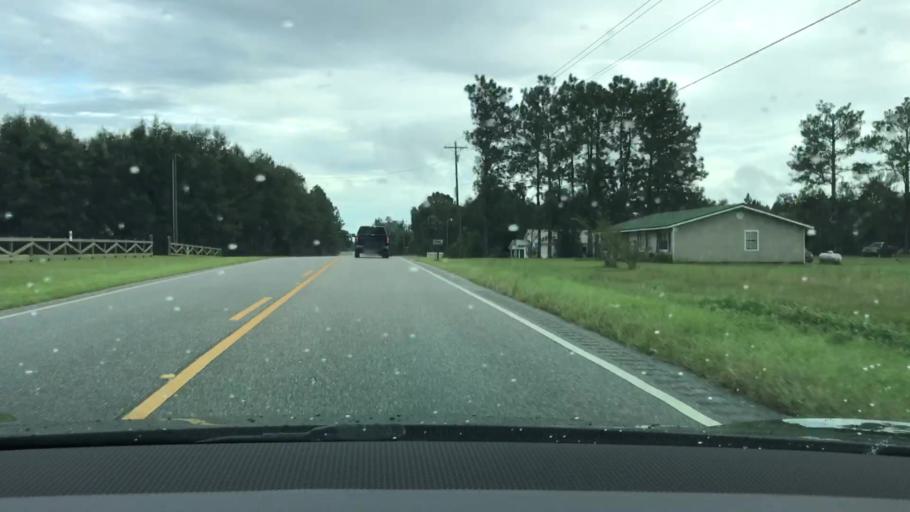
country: US
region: Alabama
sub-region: Geneva County
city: Samson
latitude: 31.0921
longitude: -86.1102
